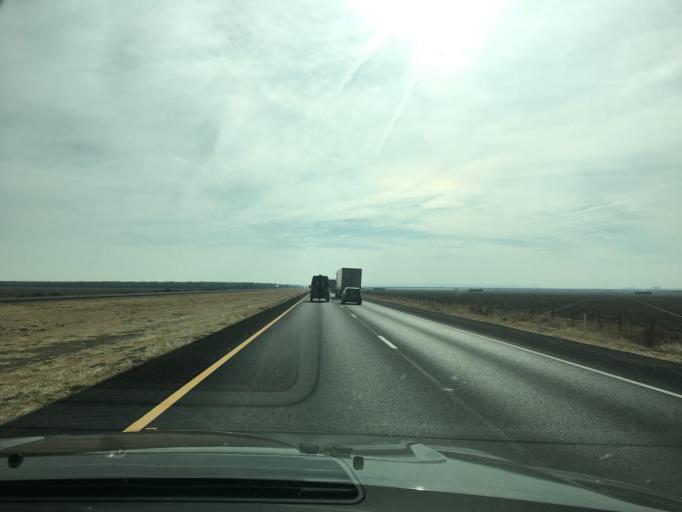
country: US
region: California
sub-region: Fresno County
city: Huron
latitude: 36.1998
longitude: -120.2097
